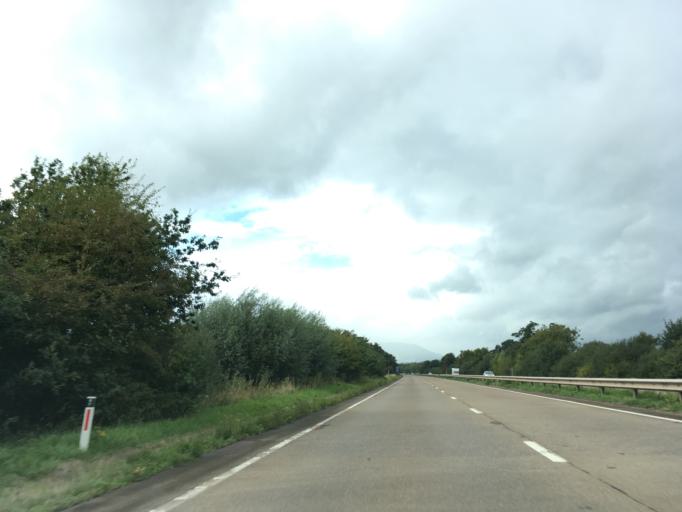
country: GB
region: Wales
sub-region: Monmouthshire
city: Llanarth
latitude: 51.7782
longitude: -2.8945
